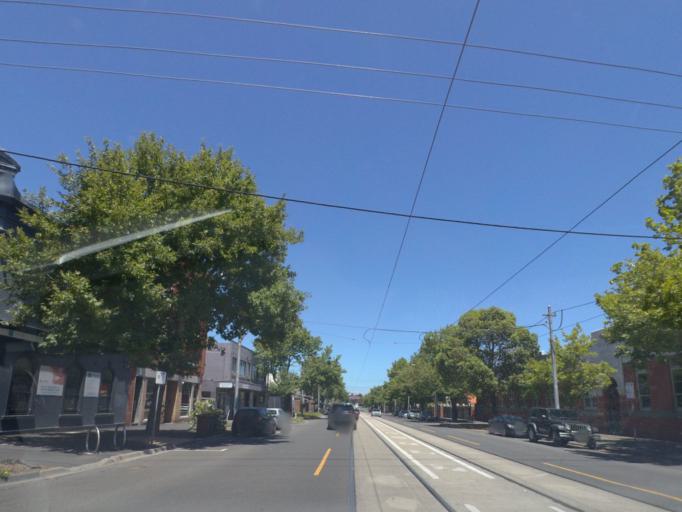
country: AU
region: Victoria
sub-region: Port Phillip
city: South Melbourne
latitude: -37.8362
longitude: 144.9621
